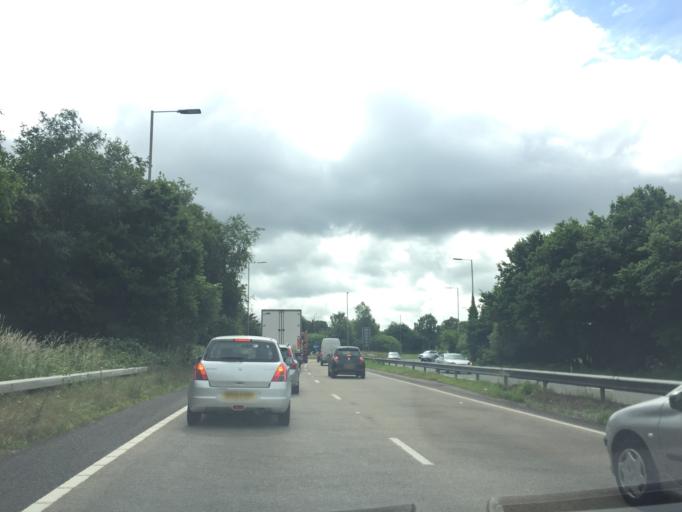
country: GB
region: England
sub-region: Dorset
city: Ferndown
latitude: 50.8137
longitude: -1.8741
